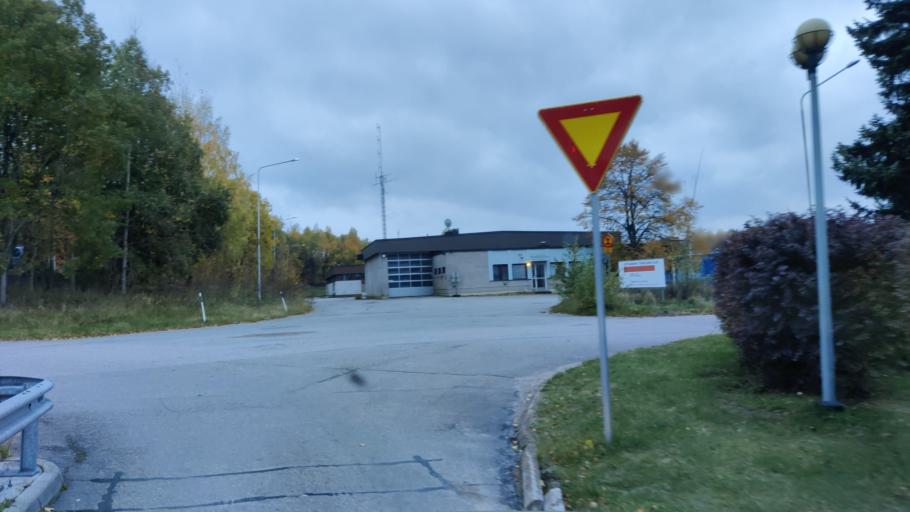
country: FI
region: Uusimaa
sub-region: Helsinki
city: Vantaa
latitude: 60.2490
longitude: 25.0458
